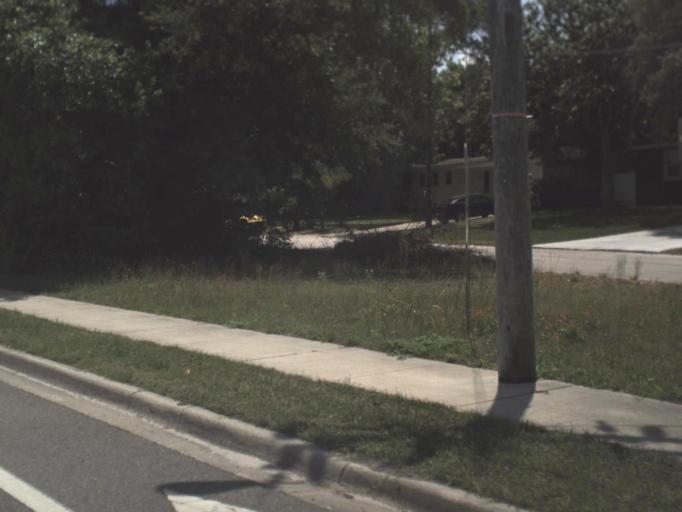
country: US
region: Florida
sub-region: Saint Johns County
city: Saint Augustine Beach
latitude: 29.8767
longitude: -81.2857
